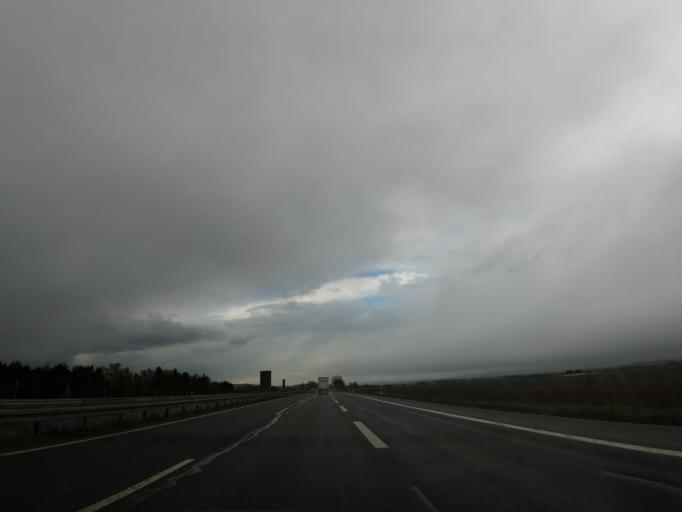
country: DE
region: Lower Saxony
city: Vienenburg
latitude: 51.9179
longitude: 10.5554
